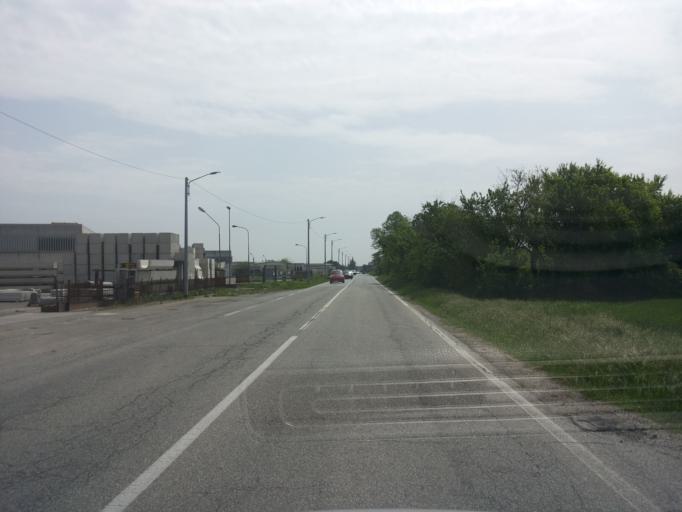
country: IT
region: Piedmont
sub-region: Provincia di Alessandria
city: Occimiano
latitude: 45.0721
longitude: 8.4899
